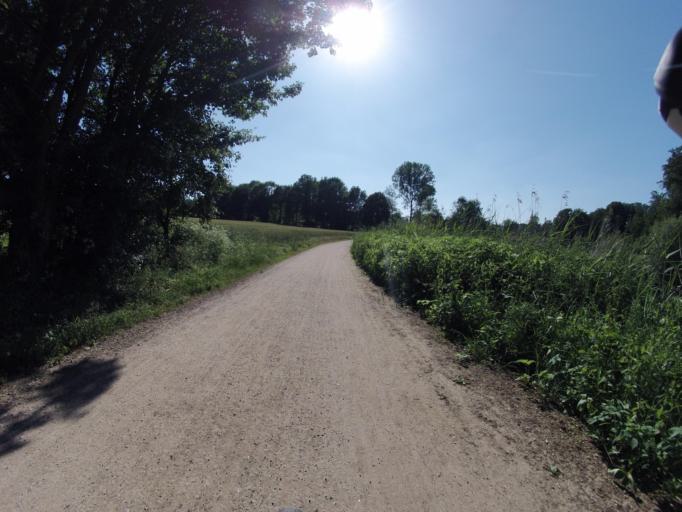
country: DE
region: North Rhine-Westphalia
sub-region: Regierungsbezirk Munster
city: Rheine
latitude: 52.3078
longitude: 7.4104
